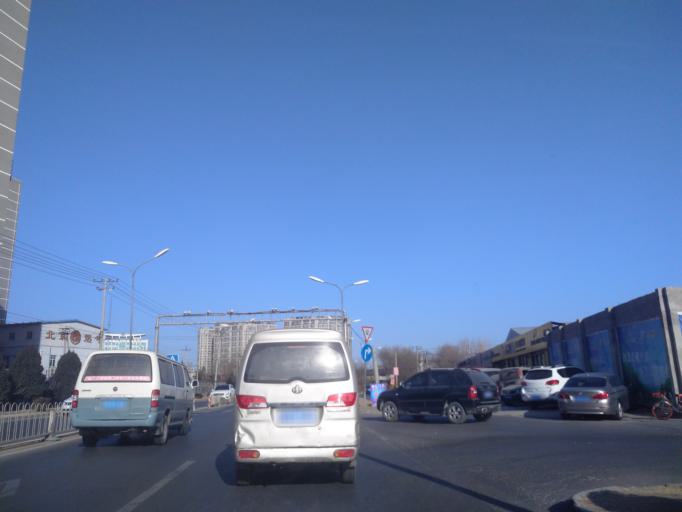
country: CN
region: Beijing
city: Jiugong
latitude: 39.8292
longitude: 116.4707
